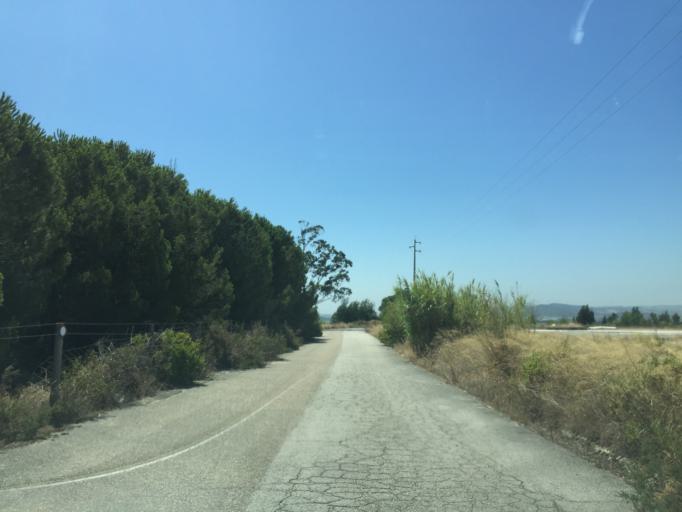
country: PT
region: Lisbon
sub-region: Alenquer
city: Carregado
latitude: 39.0478
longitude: -8.9275
